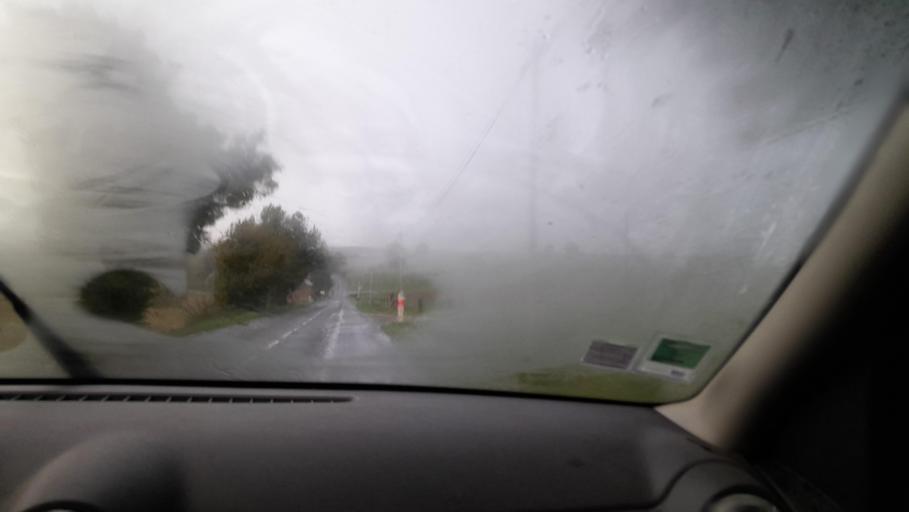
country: FR
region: Pays de la Loire
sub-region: Departement de la Mayenne
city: Ballots
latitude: 47.8626
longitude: -1.0495
